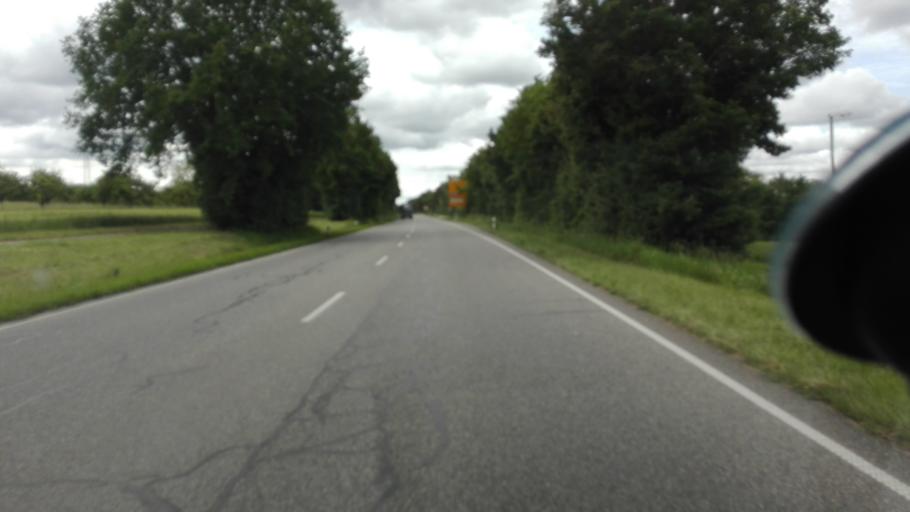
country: DE
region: Baden-Wuerttemberg
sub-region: Karlsruhe Region
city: Kronau
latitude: 49.2130
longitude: 8.6511
